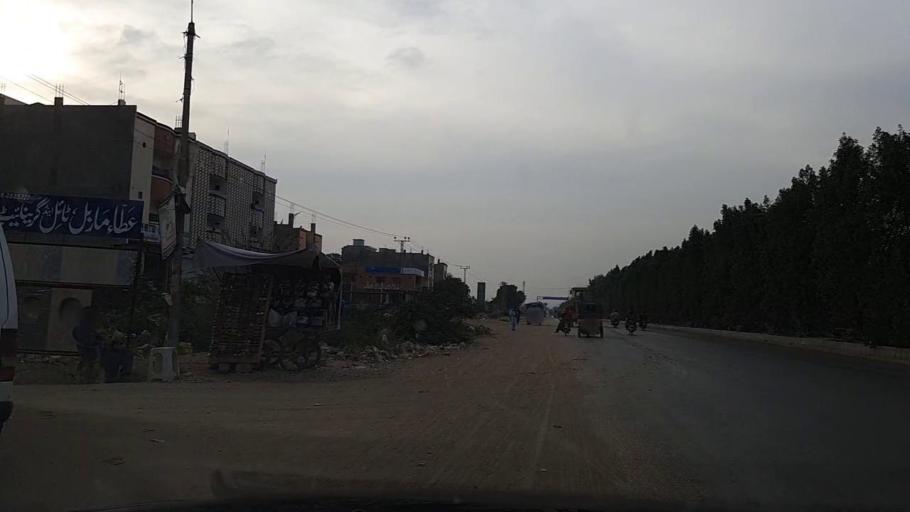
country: PK
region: Sindh
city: Malir Cantonment
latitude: 24.8603
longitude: 67.3330
